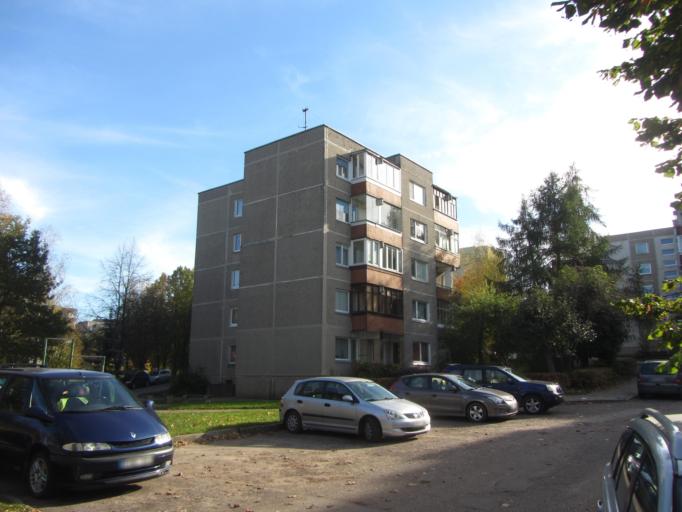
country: LT
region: Vilnius County
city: Elektrenai
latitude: 54.7881
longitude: 24.6729
